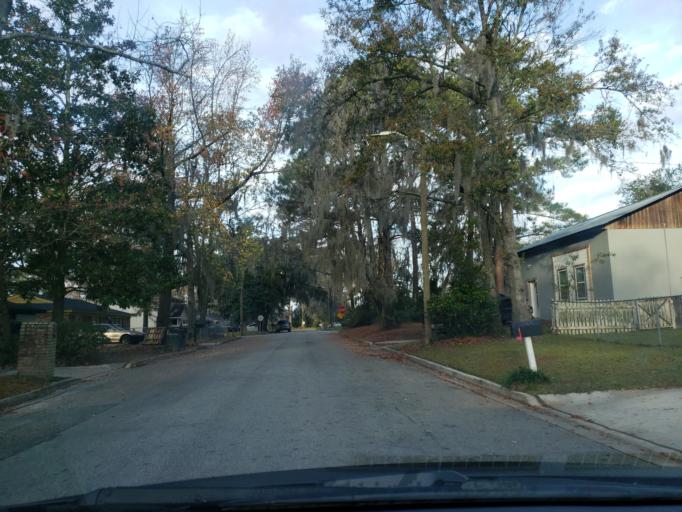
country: US
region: Georgia
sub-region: Chatham County
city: Montgomery
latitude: 31.9959
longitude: -81.1212
